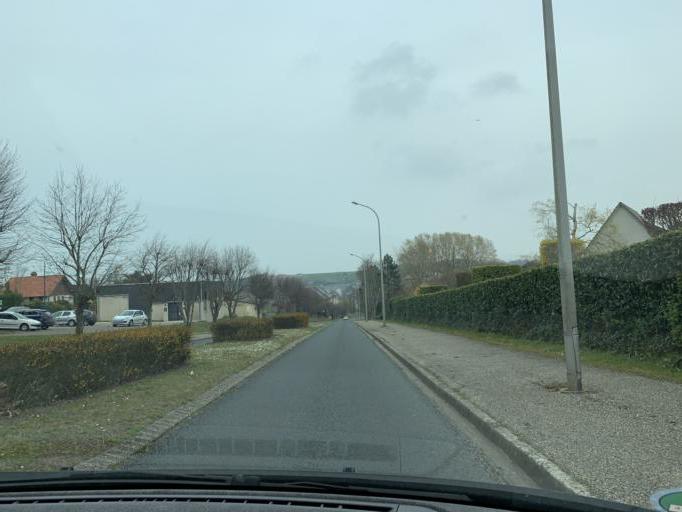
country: FR
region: Haute-Normandie
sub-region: Departement de la Seine-Maritime
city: Saint-Valery-en-Caux
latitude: 49.8619
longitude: 0.7027
